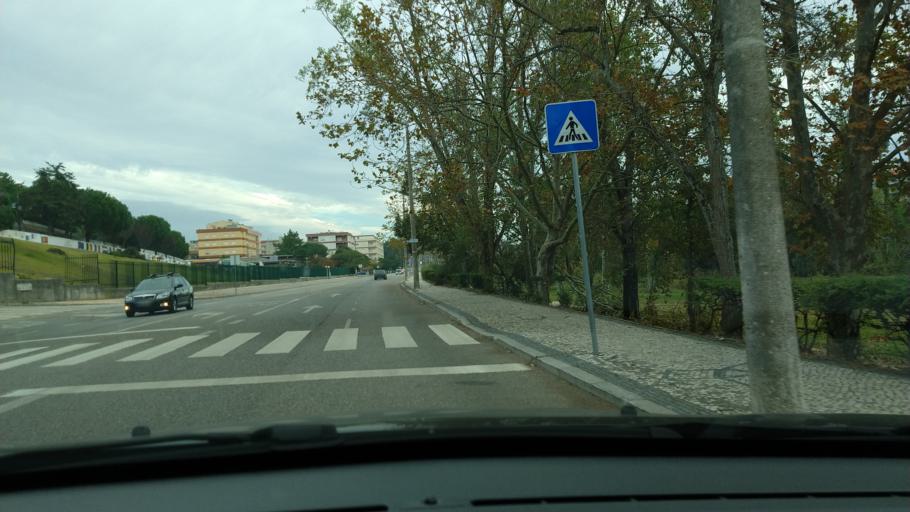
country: PT
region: Coimbra
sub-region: Figueira da Foz
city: Figueira da Foz
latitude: 40.1568
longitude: -8.8609
